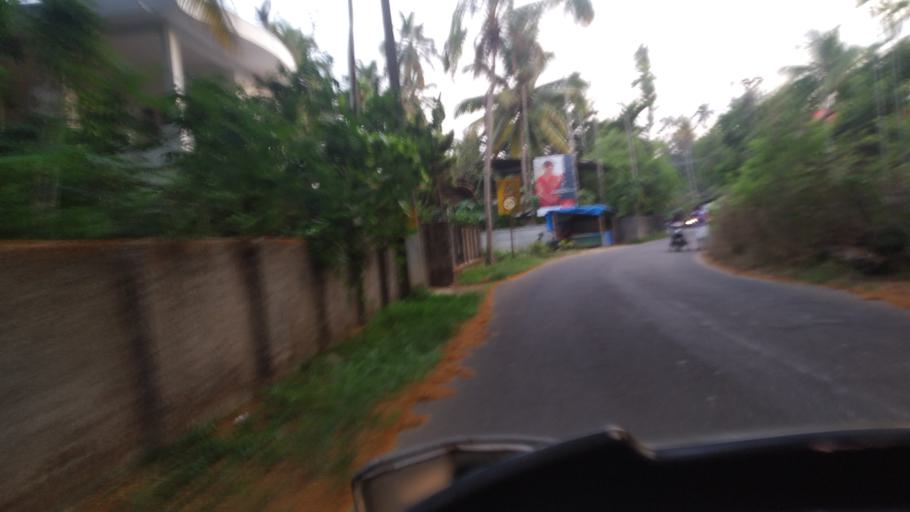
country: IN
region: Kerala
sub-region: Thrissur District
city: Kodungallur
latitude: 10.1759
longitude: 76.1991
